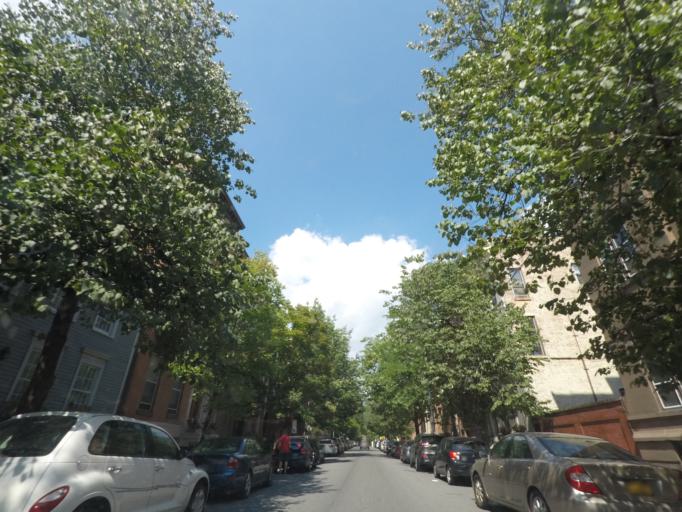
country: US
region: New York
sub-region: Rensselaer County
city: Troy
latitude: 42.7263
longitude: -73.6924
